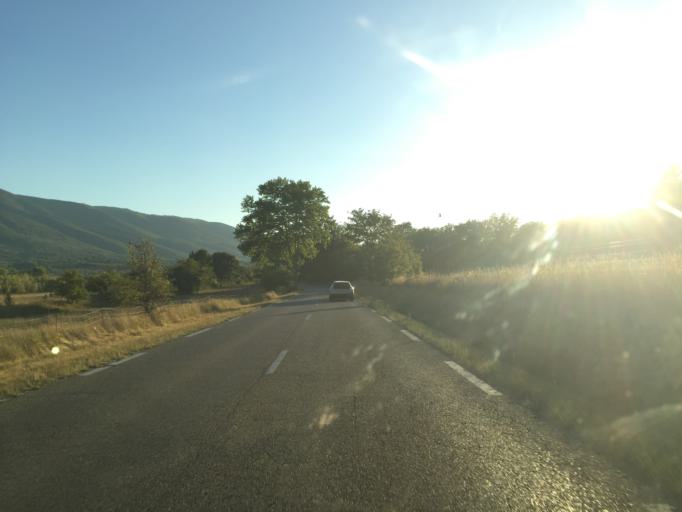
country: FR
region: Provence-Alpes-Cote d'Azur
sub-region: Departement des Alpes-de-Haute-Provence
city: Cereste
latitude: 43.8554
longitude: 5.5504
